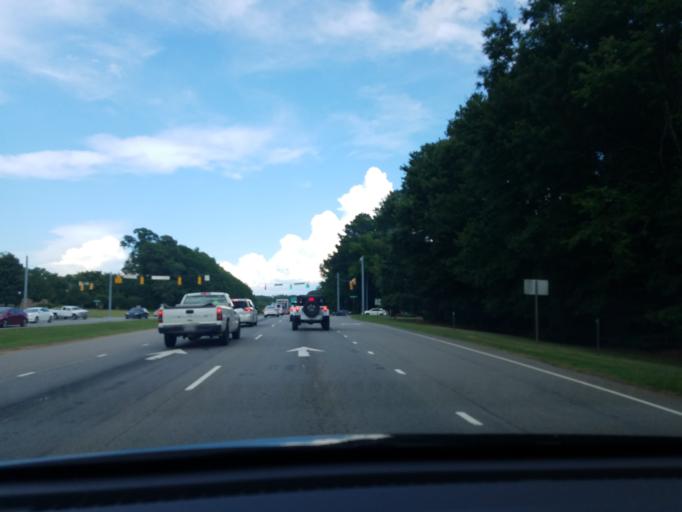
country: US
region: North Carolina
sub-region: Wake County
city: Apex
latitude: 35.7391
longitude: -78.7995
